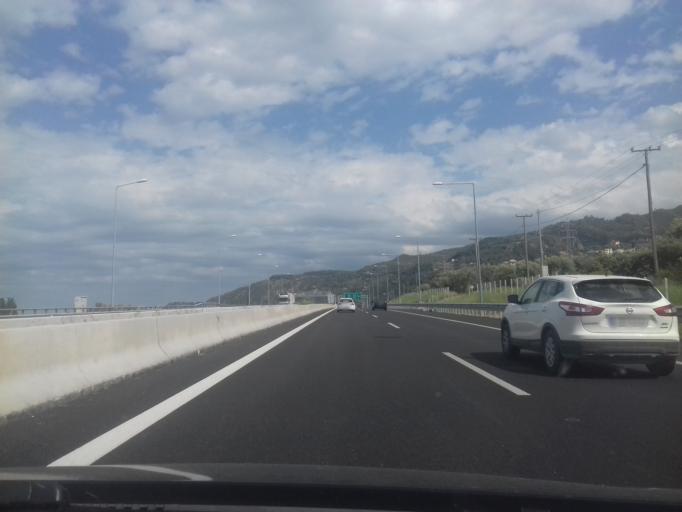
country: GR
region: West Greece
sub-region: Nomos Achaias
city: Aiyira
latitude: 38.1332
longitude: 22.3953
